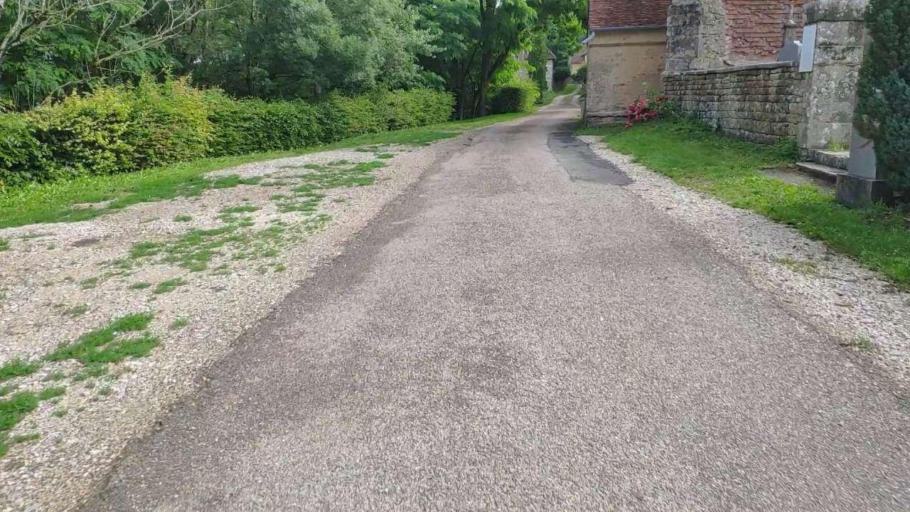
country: FR
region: Franche-Comte
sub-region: Departement du Jura
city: Poligny
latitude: 46.8266
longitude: 5.5869
